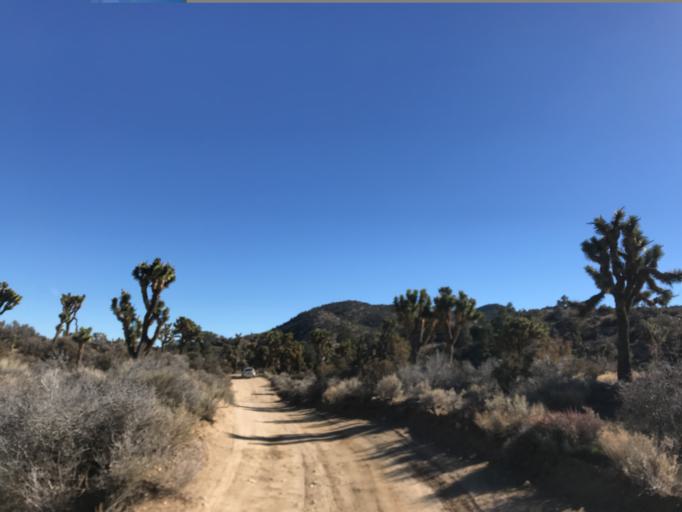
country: US
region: California
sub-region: San Bernardino County
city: Morongo Valley
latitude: 34.2264
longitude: -116.6346
